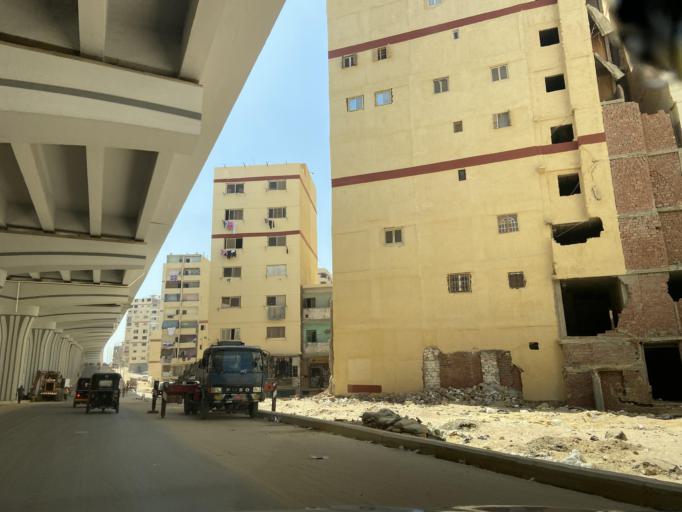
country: EG
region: Muhafazat al Qahirah
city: Cairo
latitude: 30.0654
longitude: 31.3825
